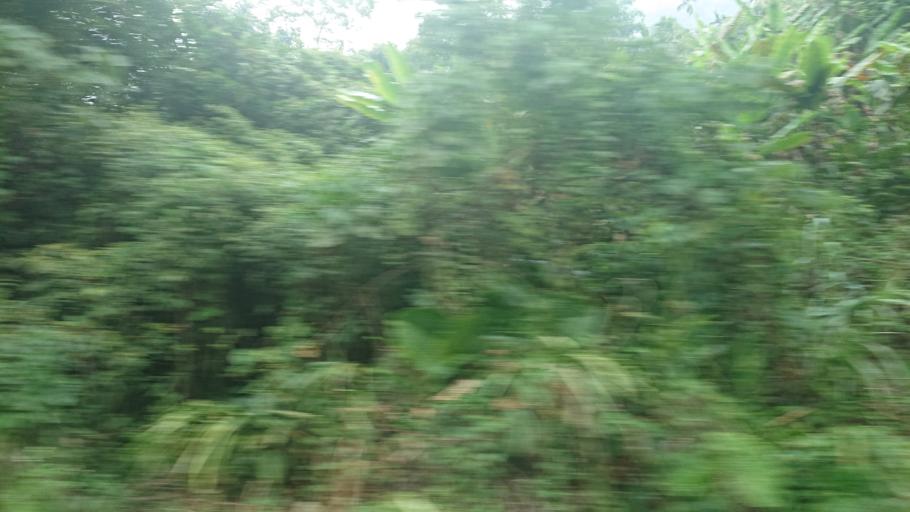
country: TW
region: Taiwan
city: Lugu
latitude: 23.5988
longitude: 120.6983
